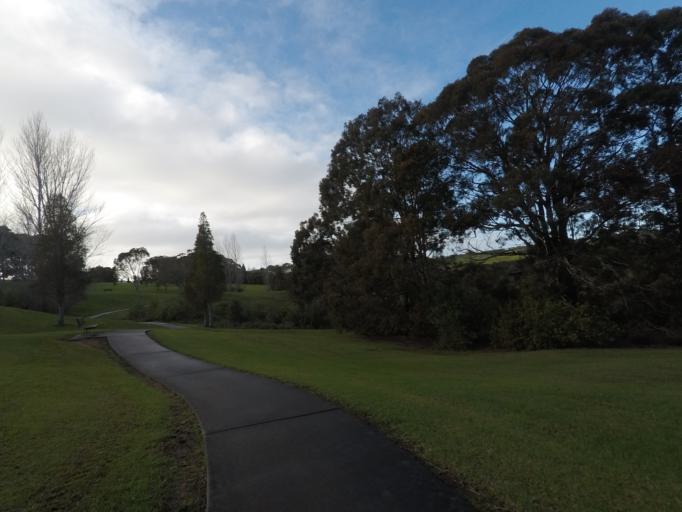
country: NZ
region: Auckland
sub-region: Auckland
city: Warkworth
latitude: -36.4230
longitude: 174.7224
